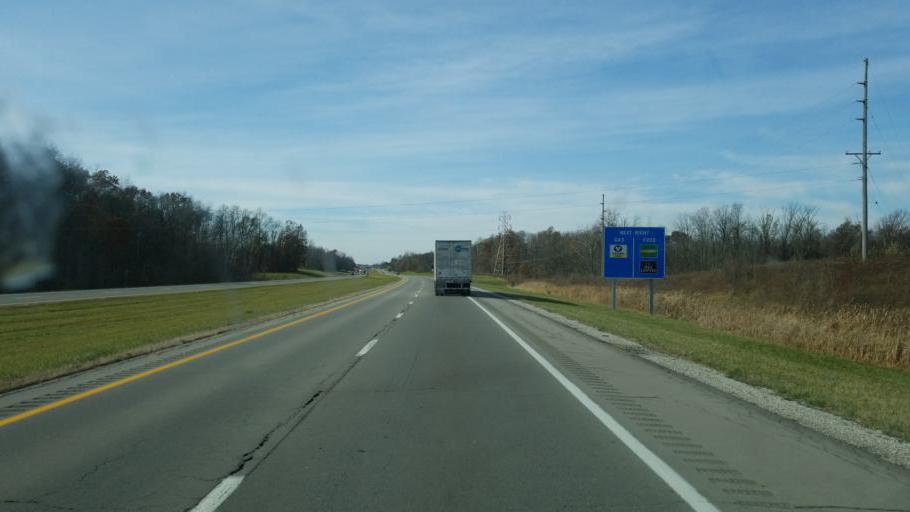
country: US
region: Ohio
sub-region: Richland County
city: Ontario
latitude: 40.7835
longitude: -82.6333
